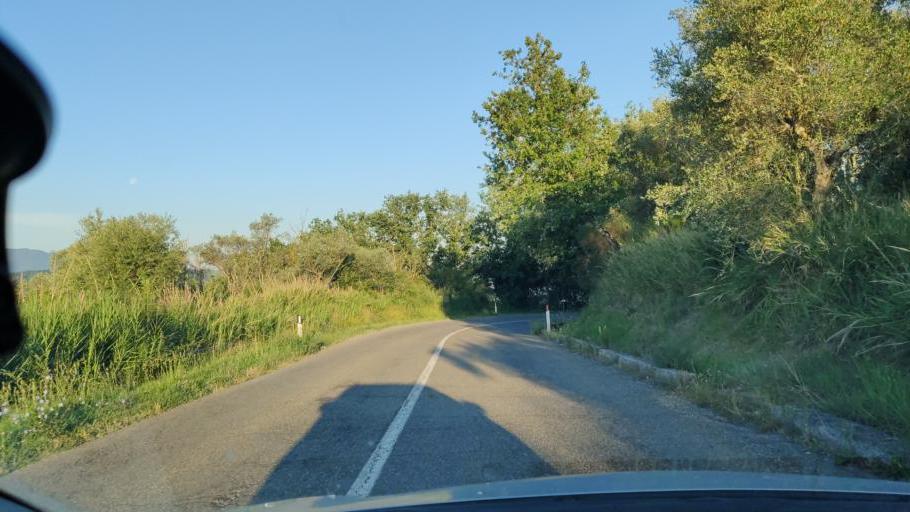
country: IT
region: Umbria
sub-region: Provincia di Terni
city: Giove
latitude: 42.5044
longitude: 12.3242
